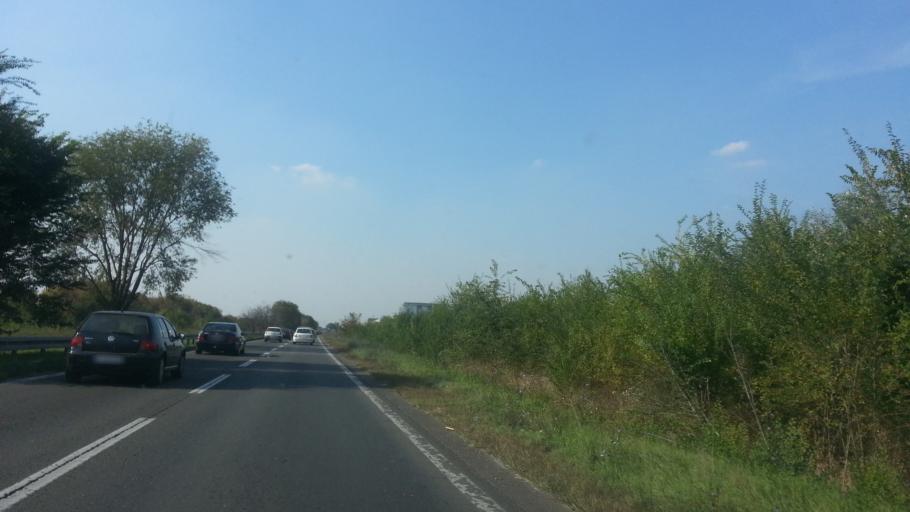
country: RS
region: Central Serbia
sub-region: Belgrade
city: Zemun
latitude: 44.8677
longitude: 20.3416
